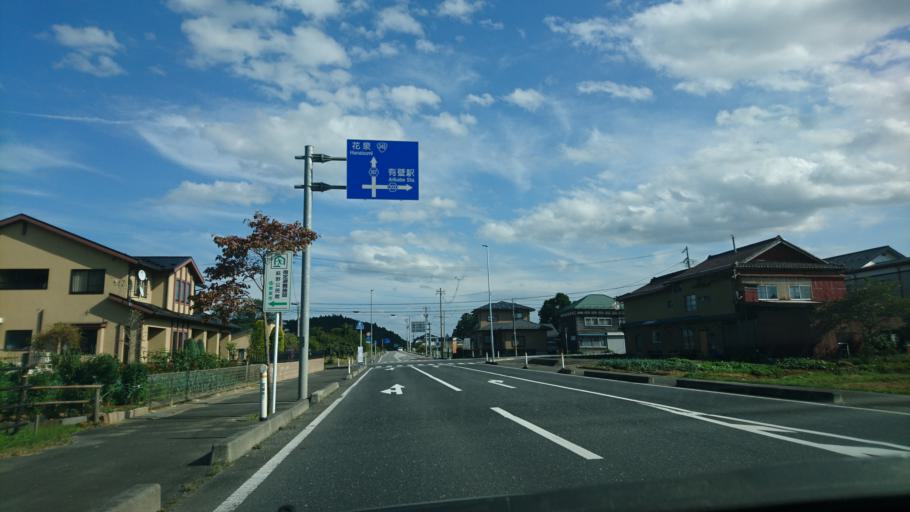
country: JP
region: Iwate
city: Ichinoseki
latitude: 38.8689
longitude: 141.1209
